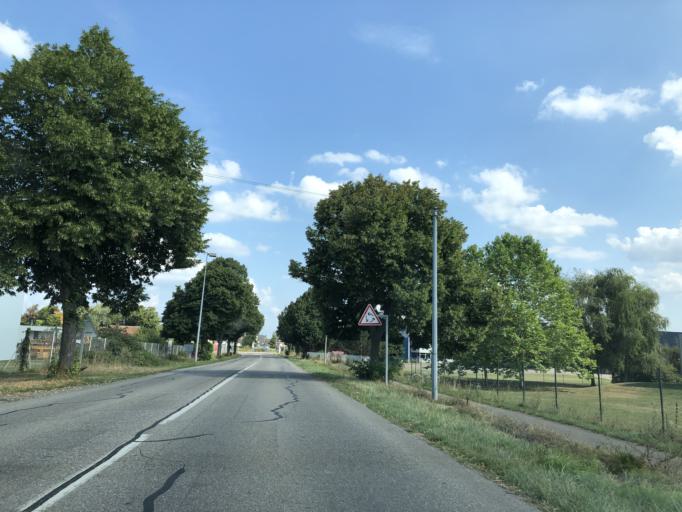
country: FR
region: Alsace
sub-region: Departement du Bas-Rhin
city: Erstein
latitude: 48.4247
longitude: 7.6331
